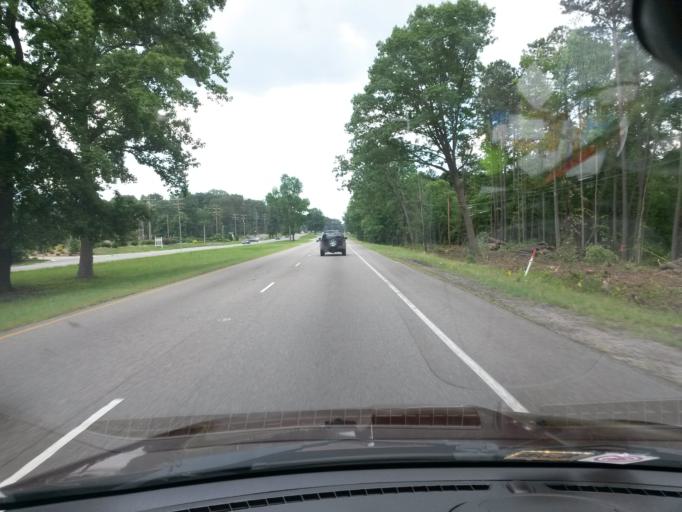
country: US
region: Virginia
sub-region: Chesterfield County
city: Enon
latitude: 37.3493
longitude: -77.3679
